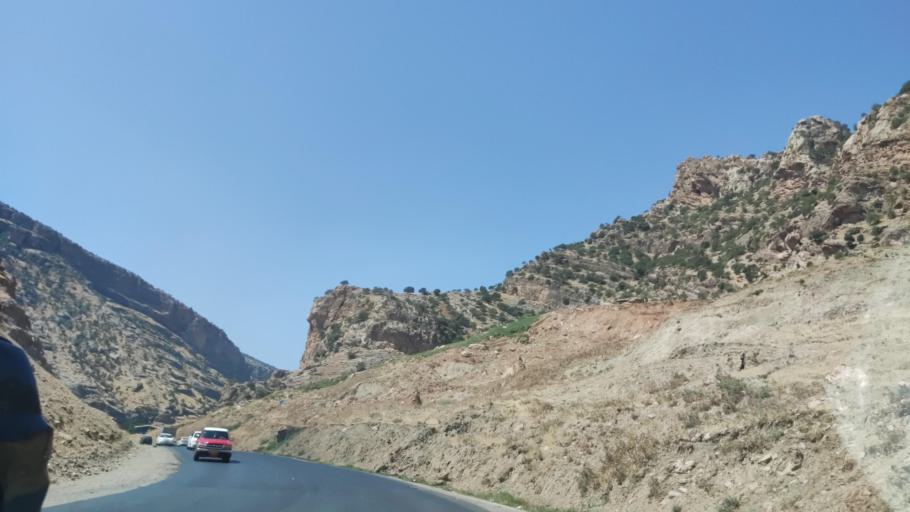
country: IQ
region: Arbil
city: Ruwandiz
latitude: 36.6330
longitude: 44.4452
